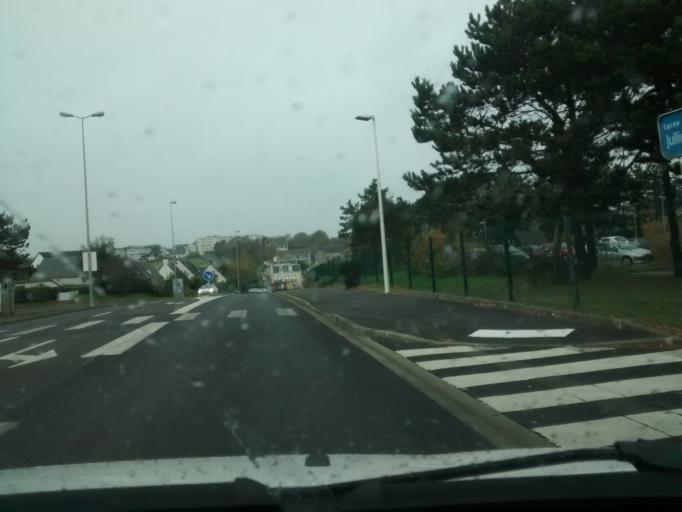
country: FR
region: Lower Normandy
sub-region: Departement de la Manche
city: Donville-les-Bains
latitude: 48.8289
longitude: -1.5802
